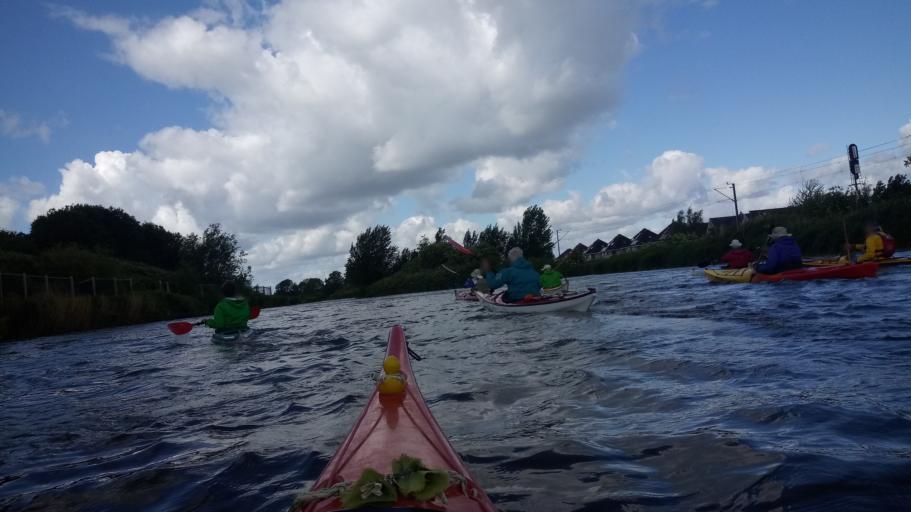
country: NL
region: North Holland
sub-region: Gemeente Enkhuizen
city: Enkhuizen
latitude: 52.6943
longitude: 5.2061
